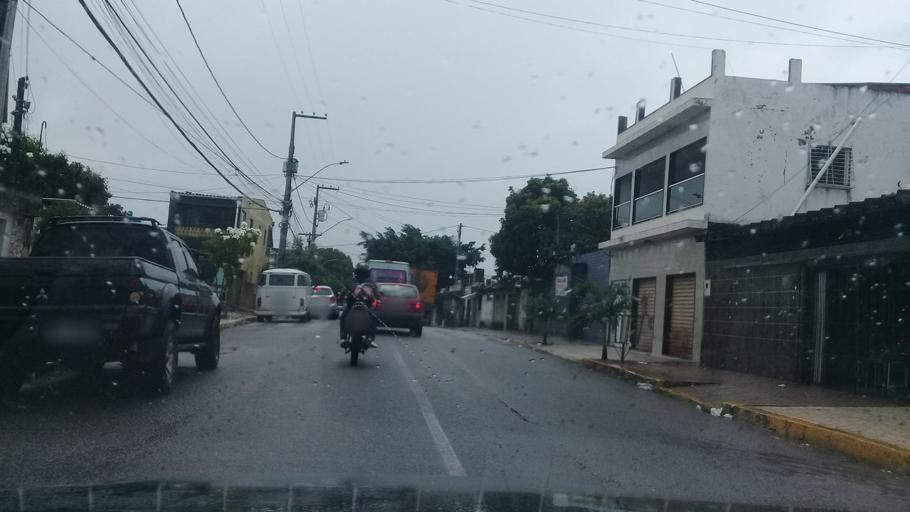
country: BR
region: Pernambuco
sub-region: Jaboatao Dos Guararapes
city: Jaboatao dos Guararapes
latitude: -8.1123
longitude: -34.9500
